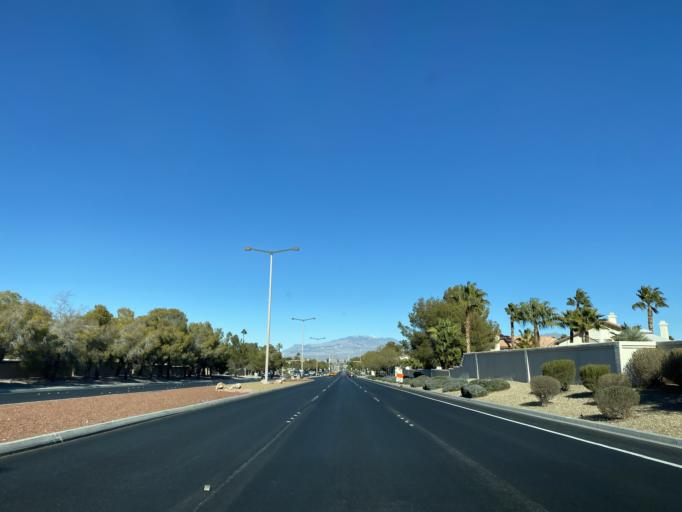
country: US
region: Nevada
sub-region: Clark County
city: Summerlin South
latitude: 36.2079
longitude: -115.2789
